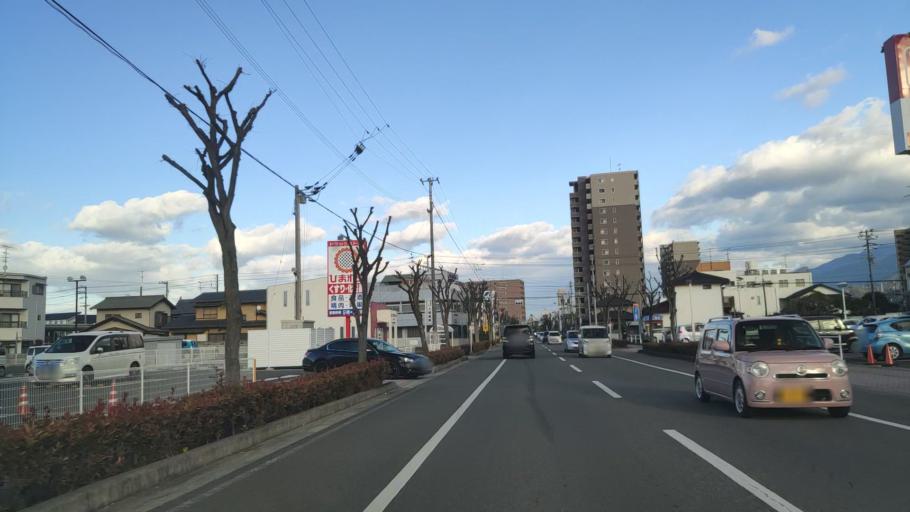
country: JP
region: Ehime
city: Saijo
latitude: 33.9171
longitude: 133.1795
